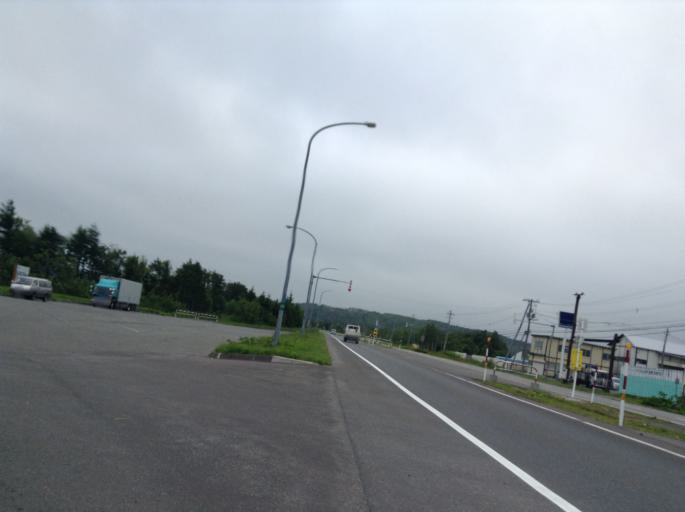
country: JP
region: Hokkaido
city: Wakkanai
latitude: 45.3643
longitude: 141.7292
